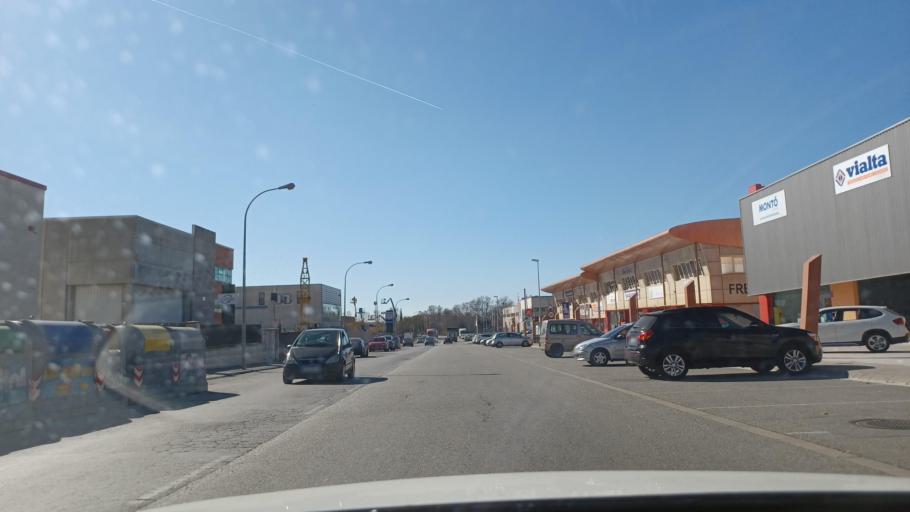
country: ES
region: Catalonia
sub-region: Provincia de Barcelona
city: Vilafranca del Penedes
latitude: 41.3385
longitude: 1.6865
